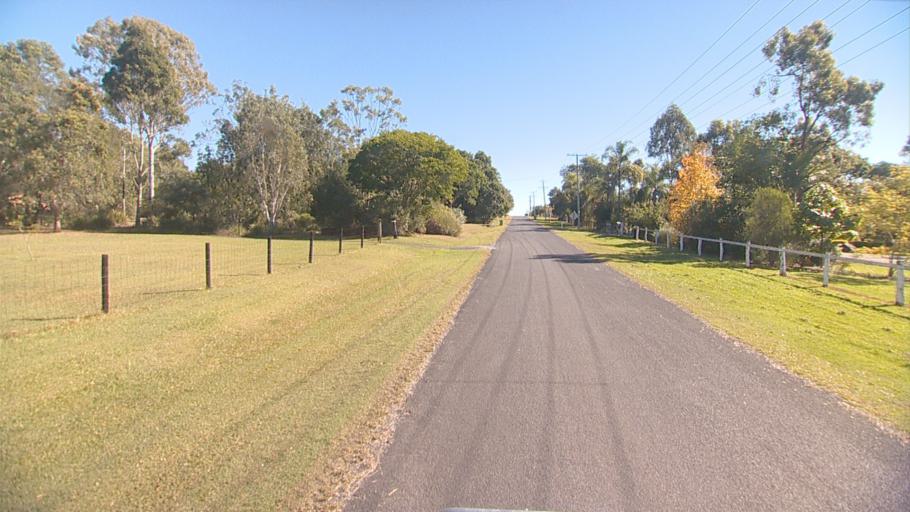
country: AU
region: Queensland
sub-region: Logan
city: Park Ridge South
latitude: -27.7236
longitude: 153.0420
